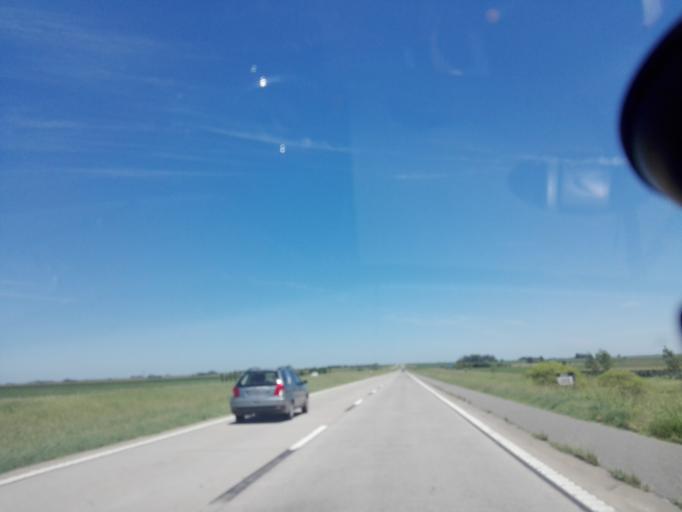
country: AR
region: Santa Fe
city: Canada de Gomez
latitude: -32.8322
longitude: -61.4737
